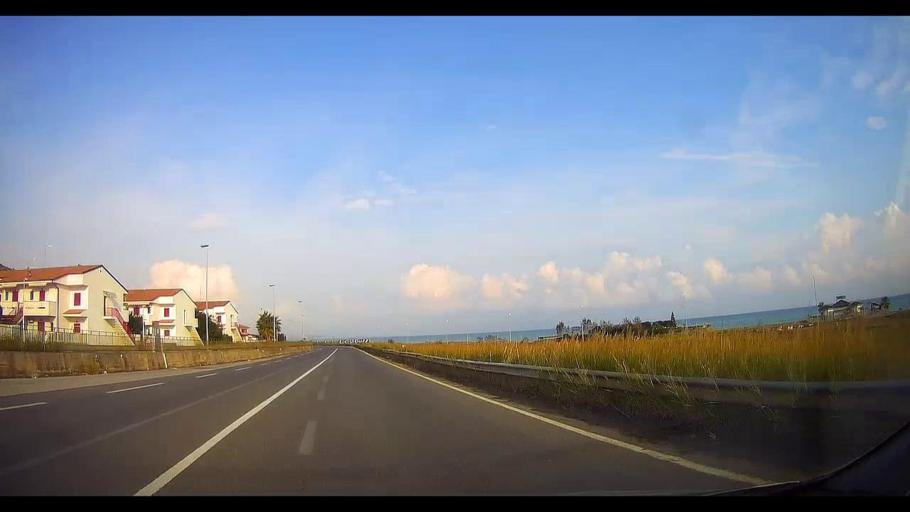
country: IT
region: Calabria
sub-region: Provincia di Cosenza
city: Cariati
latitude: 39.5266
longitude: 16.8887
